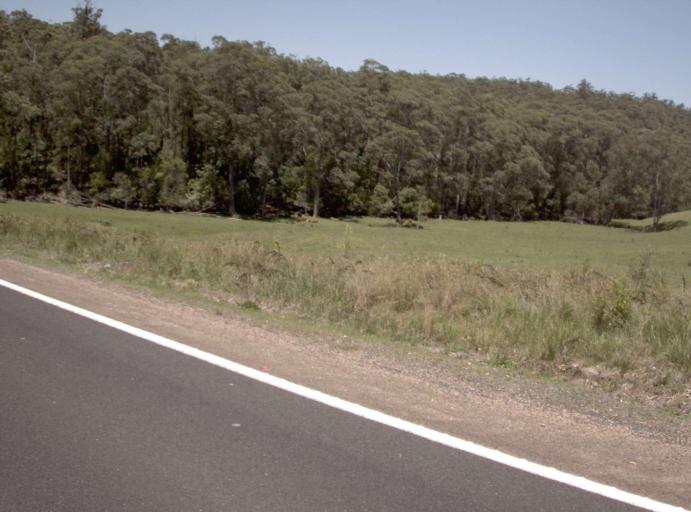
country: AU
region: Victoria
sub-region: East Gippsland
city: Lakes Entrance
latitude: -37.7068
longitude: 148.5710
